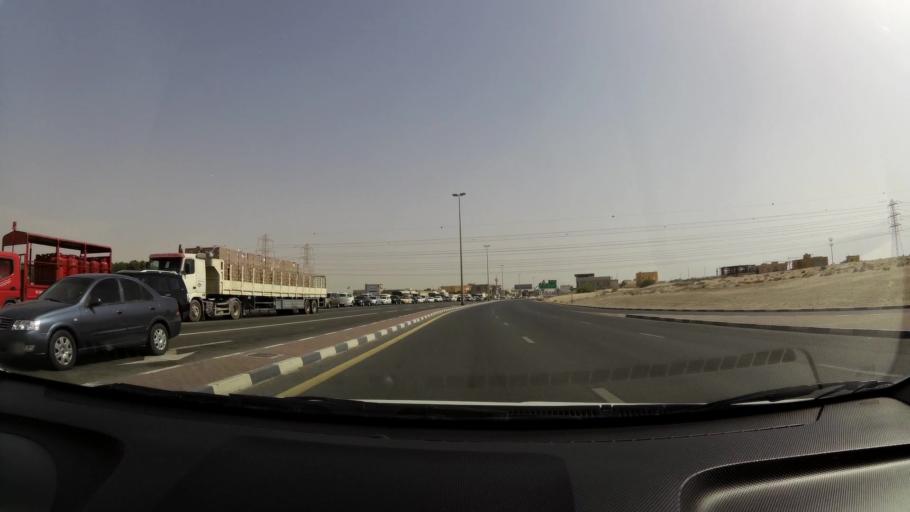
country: AE
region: Ash Shariqah
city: Sharjah
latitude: 25.2708
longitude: 55.3958
